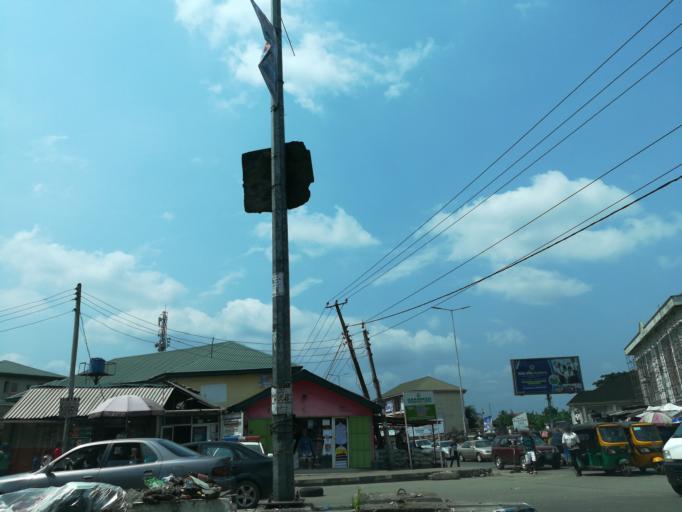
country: NG
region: Rivers
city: Port Harcourt
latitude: 4.8114
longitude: 6.9809
